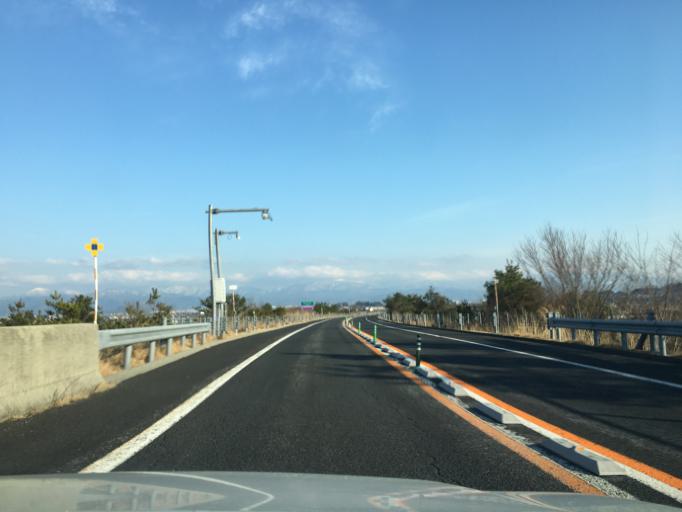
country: JP
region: Yamagata
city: Sagae
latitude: 38.3797
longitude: 140.2386
